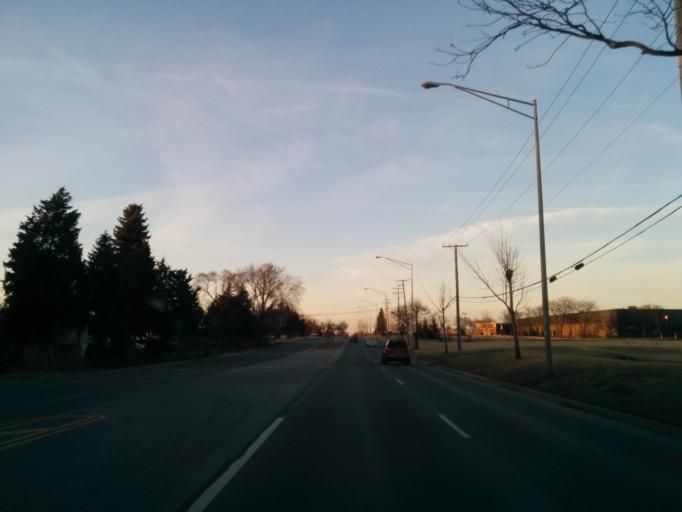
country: US
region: Illinois
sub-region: DuPage County
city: Glendale Heights
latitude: 41.9227
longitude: -88.0423
